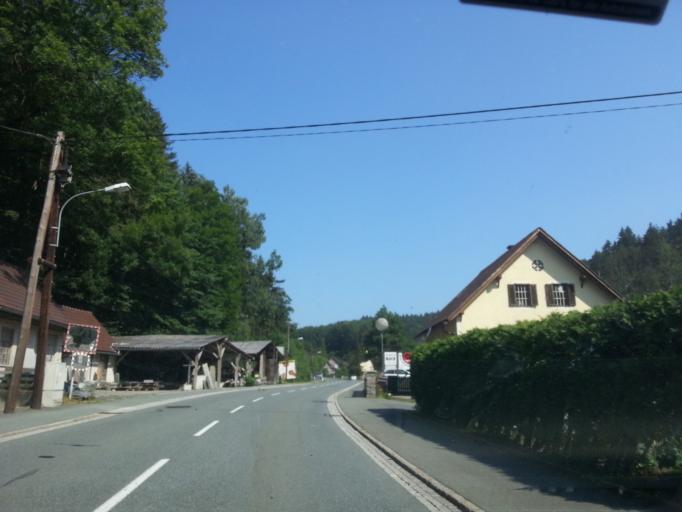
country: AT
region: Styria
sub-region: Politischer Bezirk Leibnitz
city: Grossklein
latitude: 46.7359
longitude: 15.4463
